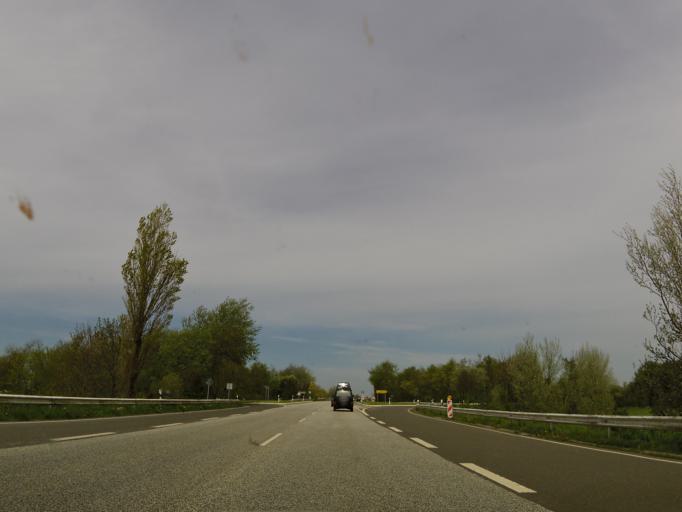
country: DE
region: Schleswig-Holstein
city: Tonning
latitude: 54.3064
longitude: 8.9602
